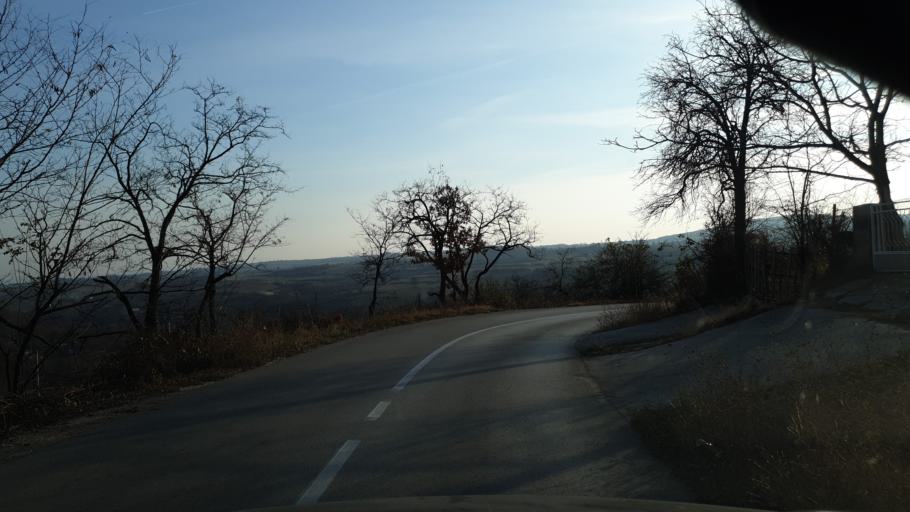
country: RS
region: Central Serbia
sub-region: Borski Okrug
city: Bor
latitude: 44.0478
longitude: 22.0841
